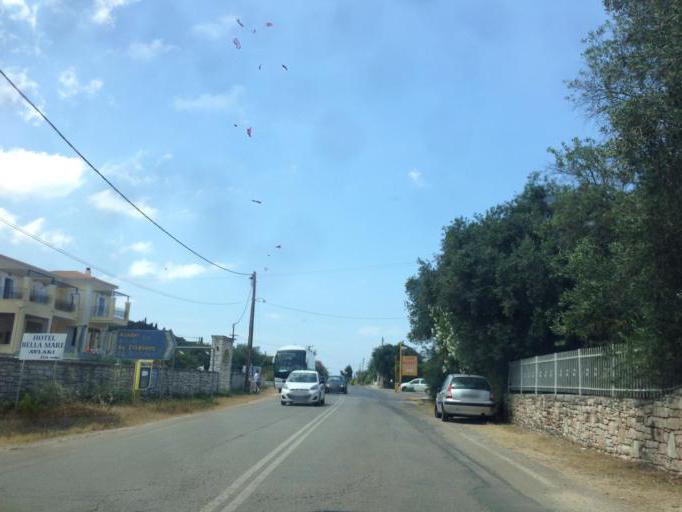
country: GR
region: Ionian Islands
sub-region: Nomos Kerkyras
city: Acharavi
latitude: 39.7825
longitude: 19.9241
